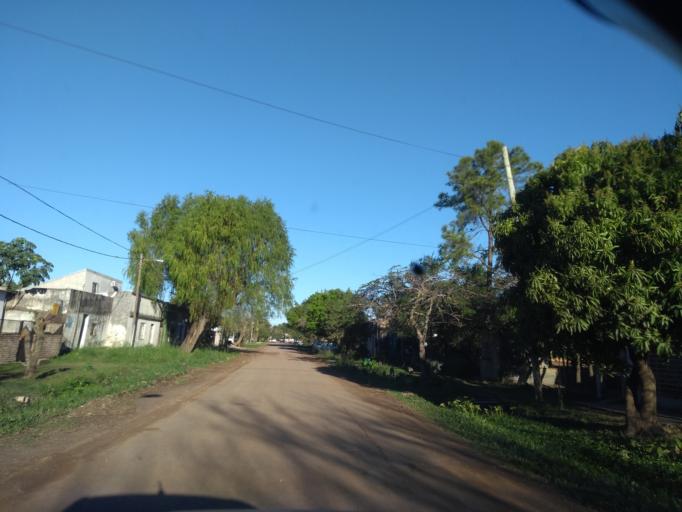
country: AR
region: Chaco
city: Barranqueras
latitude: -27.4871
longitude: -58.9442
